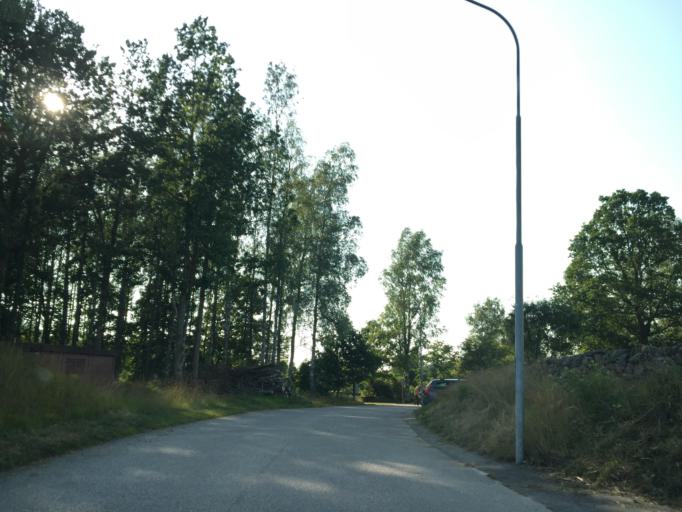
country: SE
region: Vaestra Goetaland
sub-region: Lilla Edets Kommun
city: Lilla Edet
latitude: 58.1781
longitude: 12.1030
